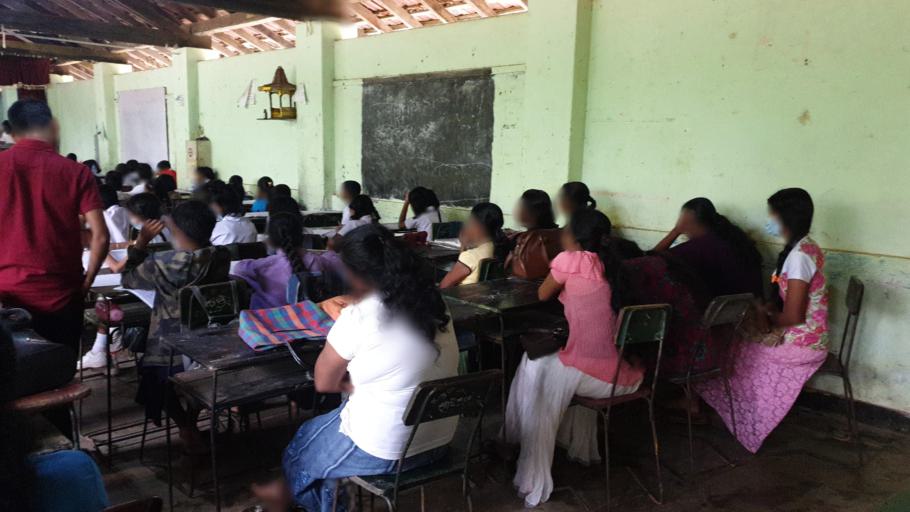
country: LK
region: Sabaragamuwa
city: Ratnapura
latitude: 6.4240
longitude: 80.5179
